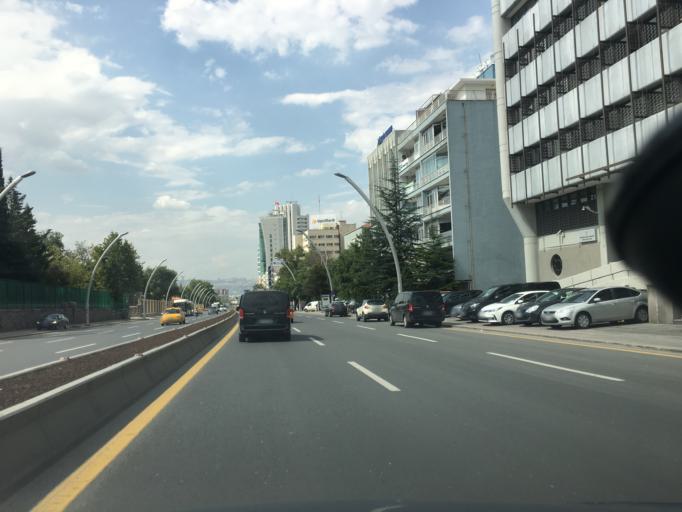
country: TR
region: Ankara
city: Cankaya
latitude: 39.9046
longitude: 32.8584
